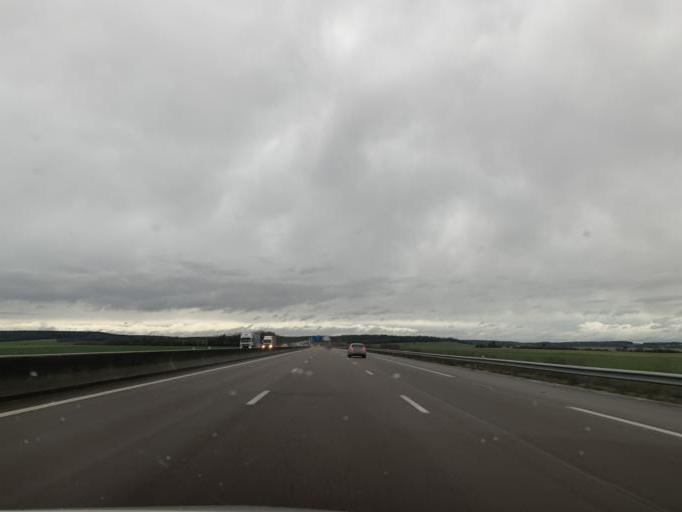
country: FR
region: Bourgogne
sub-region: Departement de la Cote-d'Or
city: Selongey
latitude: 47.5325
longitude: 5.1992
